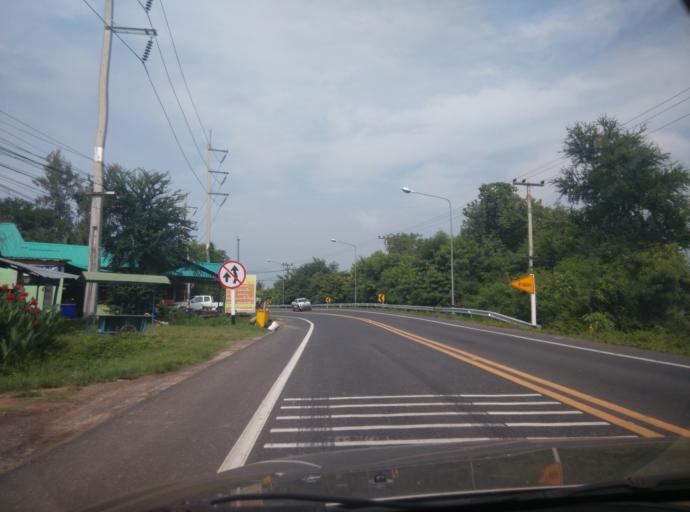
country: TH
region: Sisaket
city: Uthumphon Phisai
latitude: 15.1032
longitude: 104.1271
